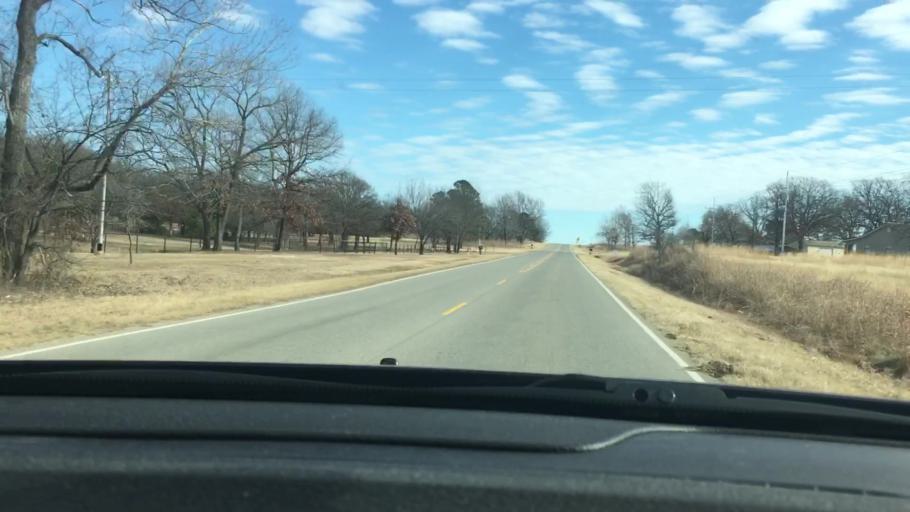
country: US
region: Oklahoma
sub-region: Pontotoc County
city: Ada
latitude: 34.7851
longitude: -96.7906
